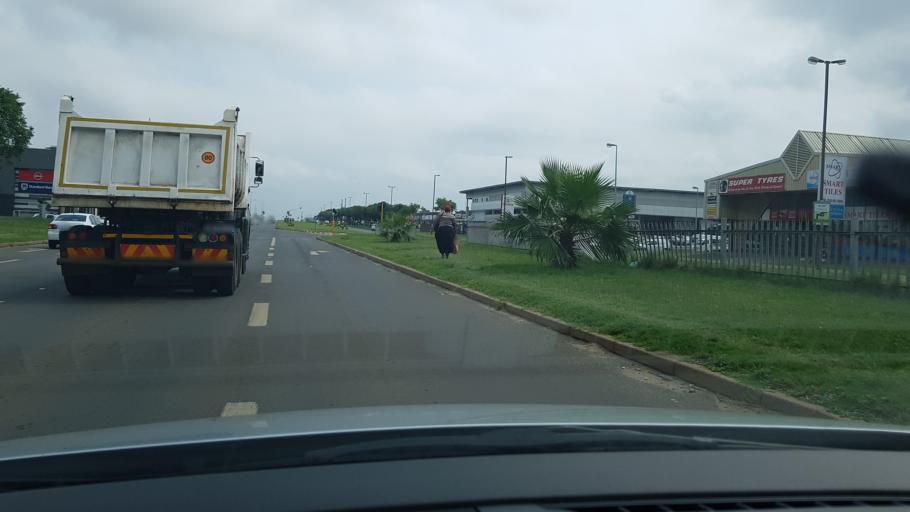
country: ZA
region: KwaZulu-Natal
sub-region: uThungulu District Municipality
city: Richards Bay
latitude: -28.7526
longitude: 32.0476
